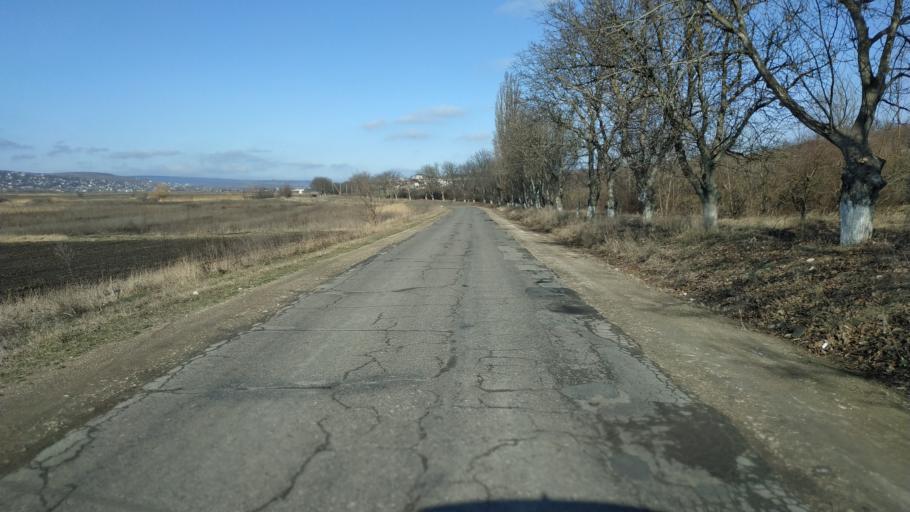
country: MD
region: Laloveni
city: Ialoveni
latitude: 46.9236
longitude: 28.6841
